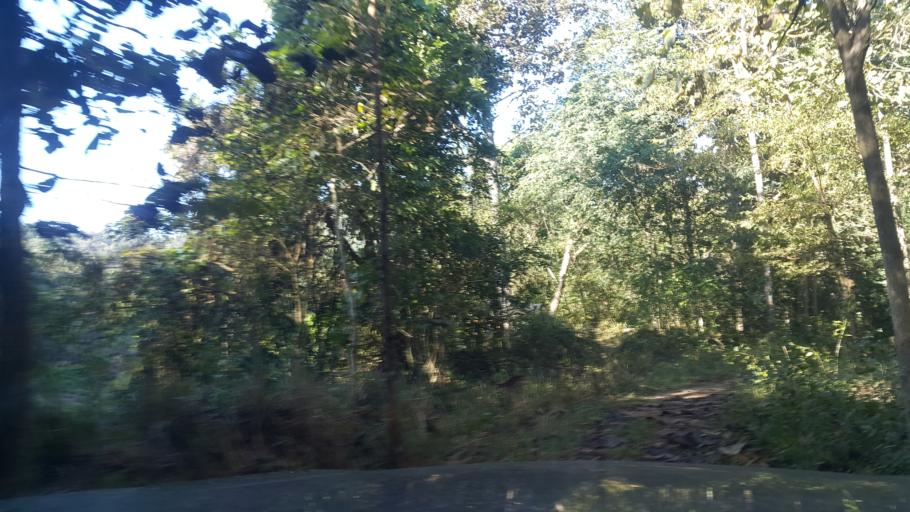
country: TH
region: Chiang Mai
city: San Kamphaeng
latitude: 18.6866
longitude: 99.2009
